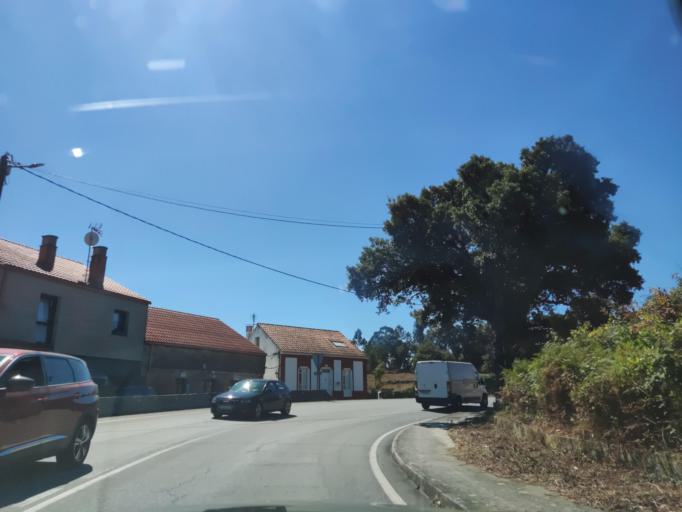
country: ES
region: Galicia
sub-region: Provincia da Coruna
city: Boiro
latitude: 42.6199
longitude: -8.9235
